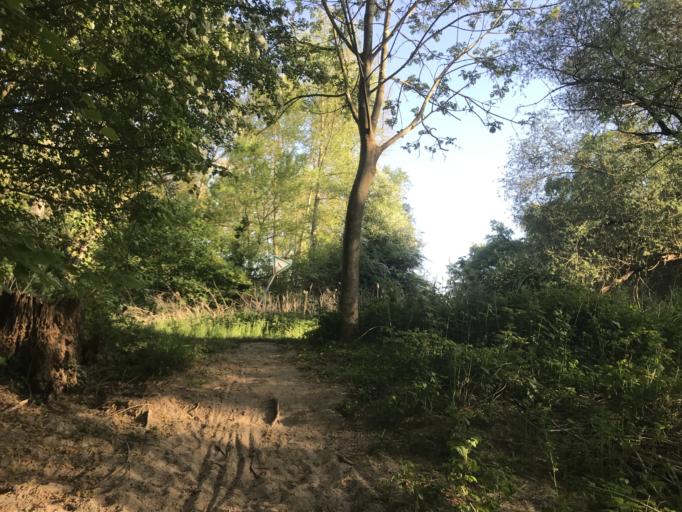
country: DE
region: Hesse
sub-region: Regierungsbezirk Darmstadt
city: Kiedrich
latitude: 50.0058
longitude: 8.0810
